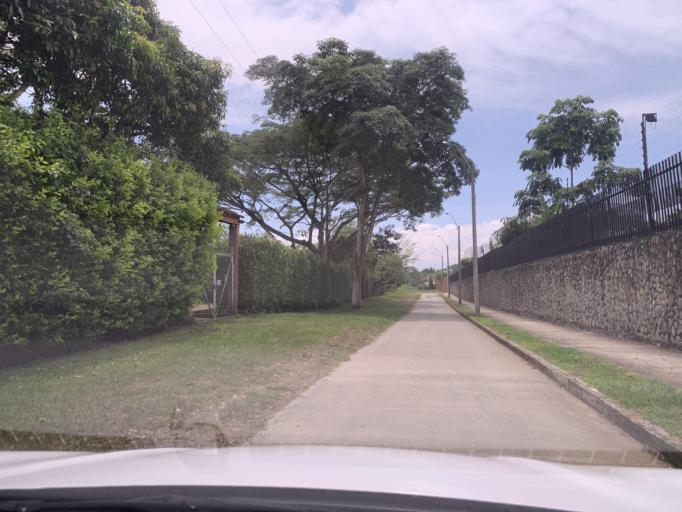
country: CO
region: Valle del Cauca
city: Jamundi
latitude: 3.3100
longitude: -76.5355
